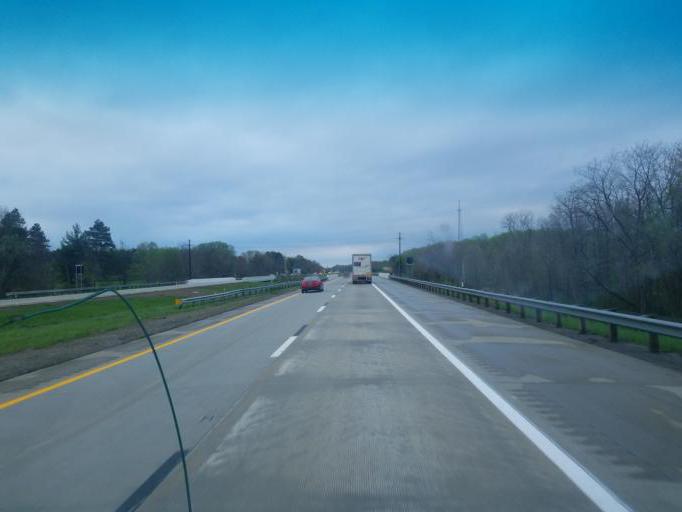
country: US
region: Ohio
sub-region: Lake County
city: Perry
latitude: 41.7186
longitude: -81.1452
